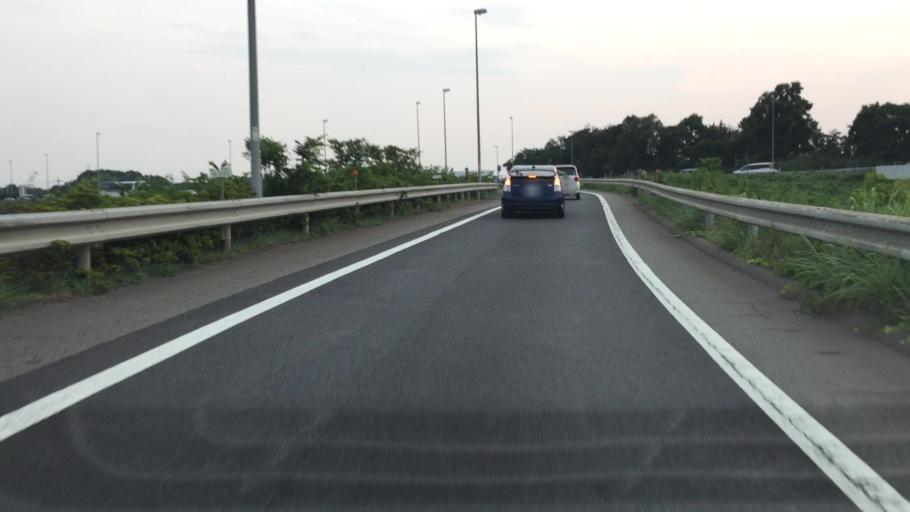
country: JP
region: Gunma
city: Tatebayashi
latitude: 36.2251
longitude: 139.5722
